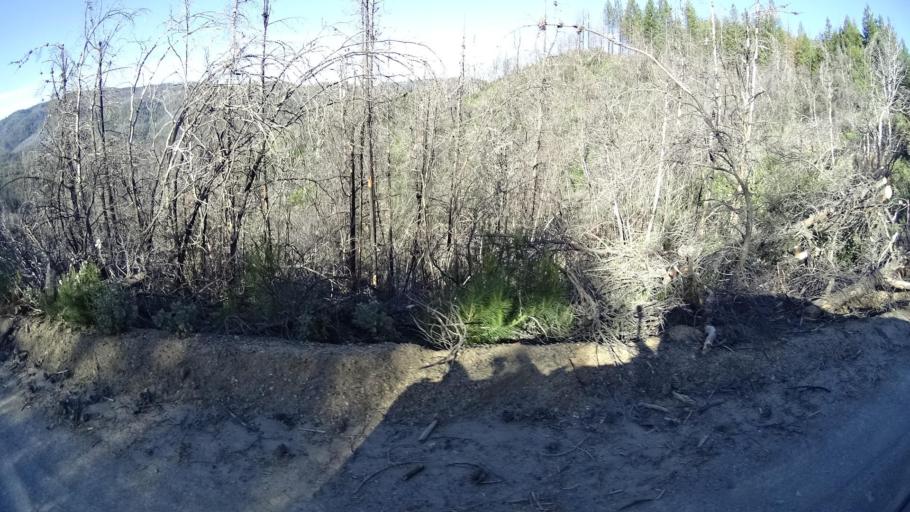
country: US
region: California
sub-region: Lake County
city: Upper Lake
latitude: 39.3457
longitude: -122.9663
